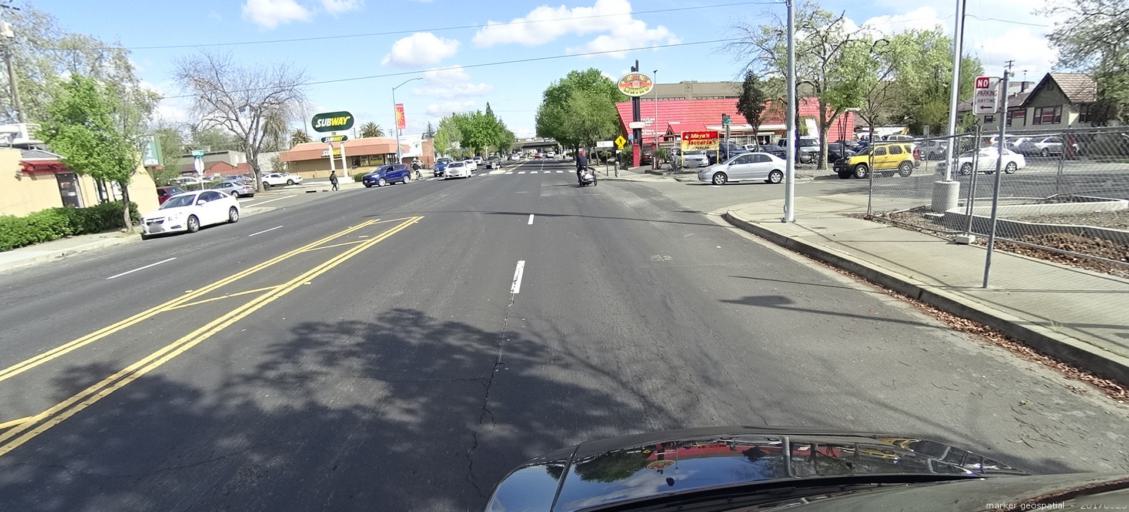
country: US
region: California
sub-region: Sacramento County
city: Sacramento
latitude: 38.5578
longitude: -121.4782
